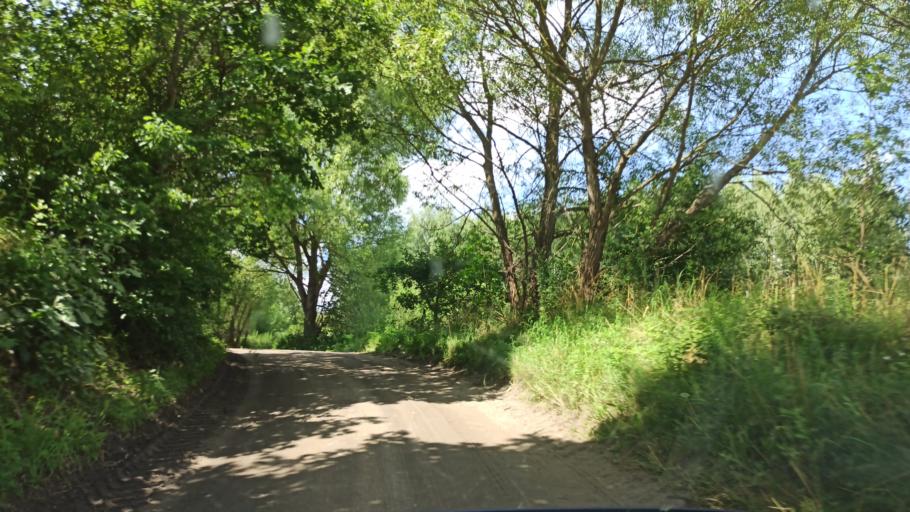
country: PL
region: Warmian-Masurian Voivodeship
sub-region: Powiat ostrodzki
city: Morag
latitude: 53.8621
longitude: 20.0612
